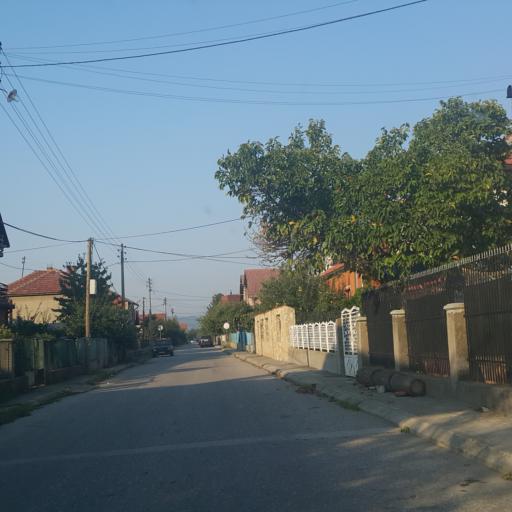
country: RS
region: Central Serbia
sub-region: Zajecarski Okrug
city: Zajecar
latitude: 43.9083
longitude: 22.2611
